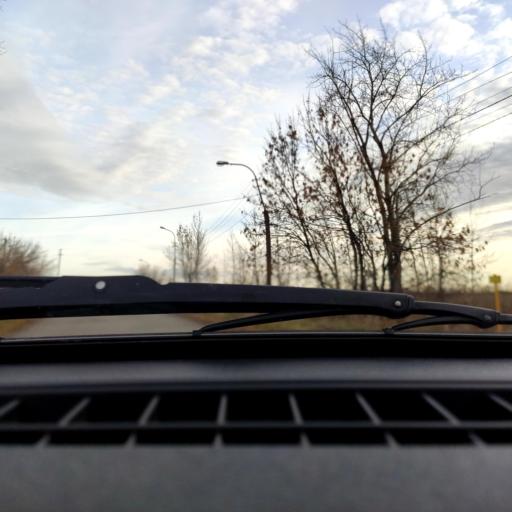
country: RU
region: Bashkortostan
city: Blagoveshchensk
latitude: 54.8997
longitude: 56.1524
